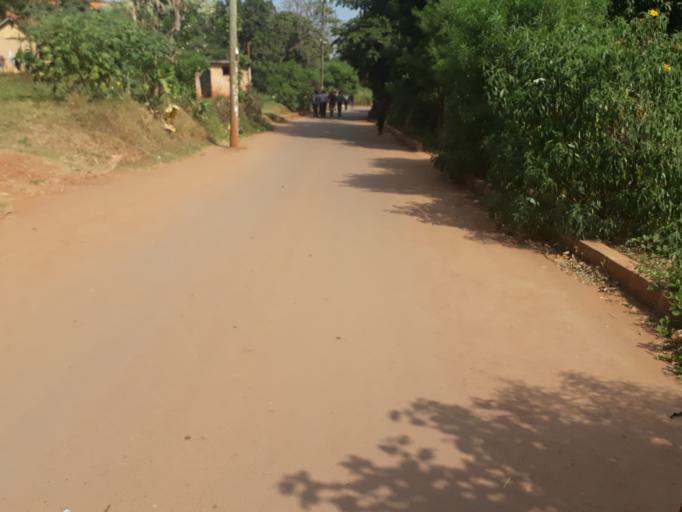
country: UG
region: Central Region
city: Kampala Central Division
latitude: 0.3331
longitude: 32.5647
